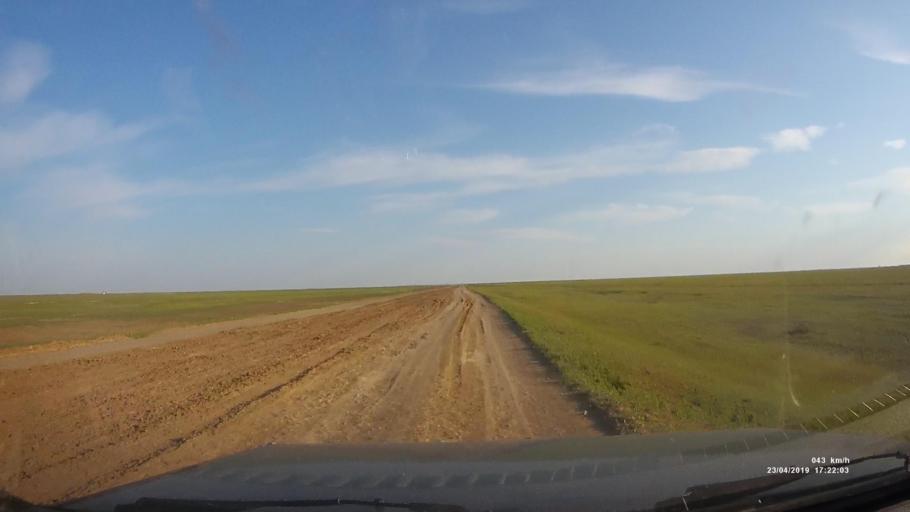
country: RU
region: Kalmykiya
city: Priyutnoye
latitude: 46.1715
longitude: 43.5061
